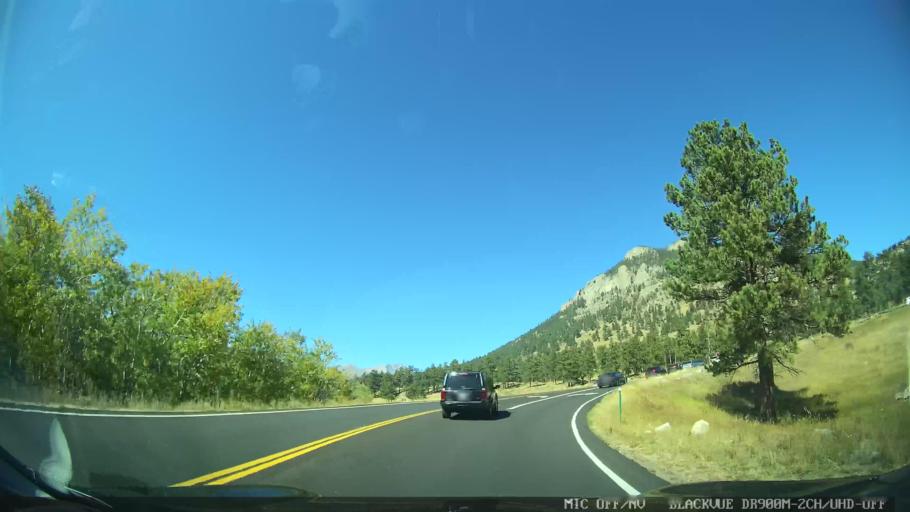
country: US
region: Colorado
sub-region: Larimer County
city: Estes Park
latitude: 40.3649
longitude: -105.5855
